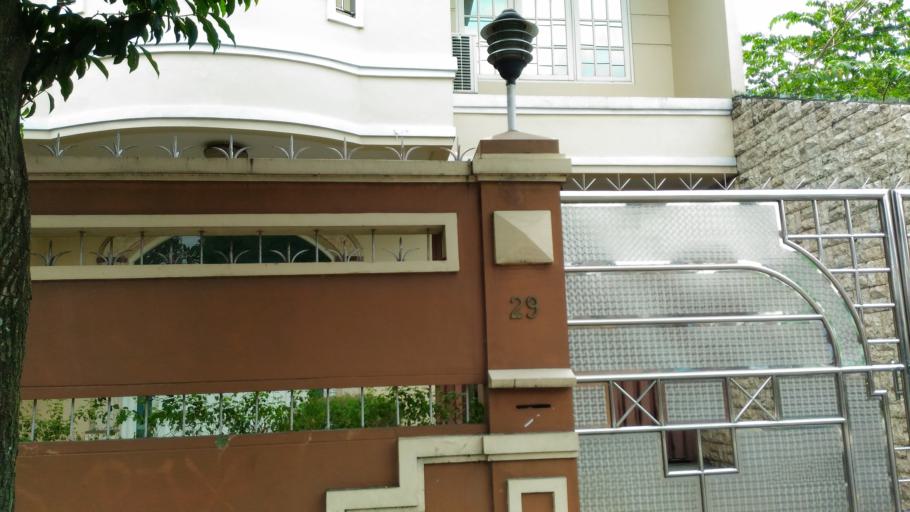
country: ID
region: Daerah Istimewa Yogyakarta
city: Yogyakarta
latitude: -7.8061
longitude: 110.3778
